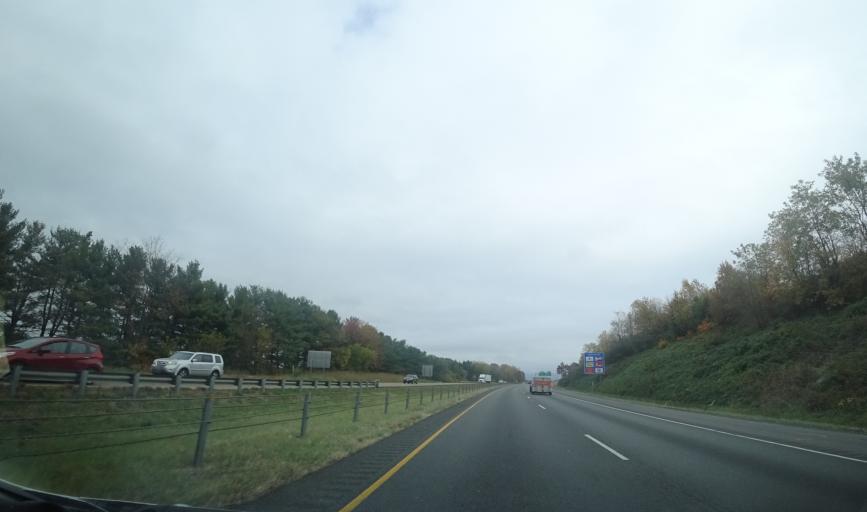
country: US
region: Virginia
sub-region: City of Harrisonburg
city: Harrisonburg
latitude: 38.4352
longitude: -78.8651
